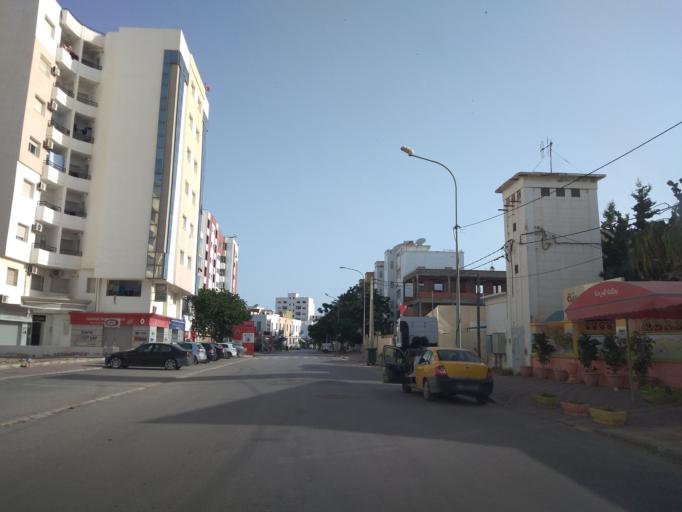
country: TN
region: Safaqis
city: Sfax
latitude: 34.7303
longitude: 10.7550
